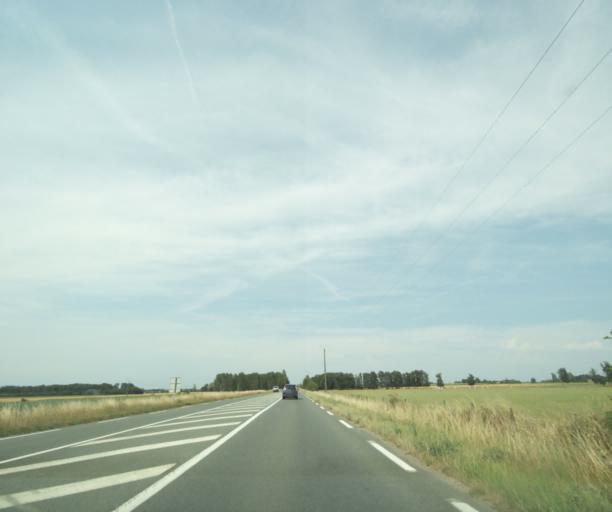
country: FR
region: Centre
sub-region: Departement d'Indre-et-Loire
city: Sorigny
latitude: 47.2119
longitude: 0.6772
